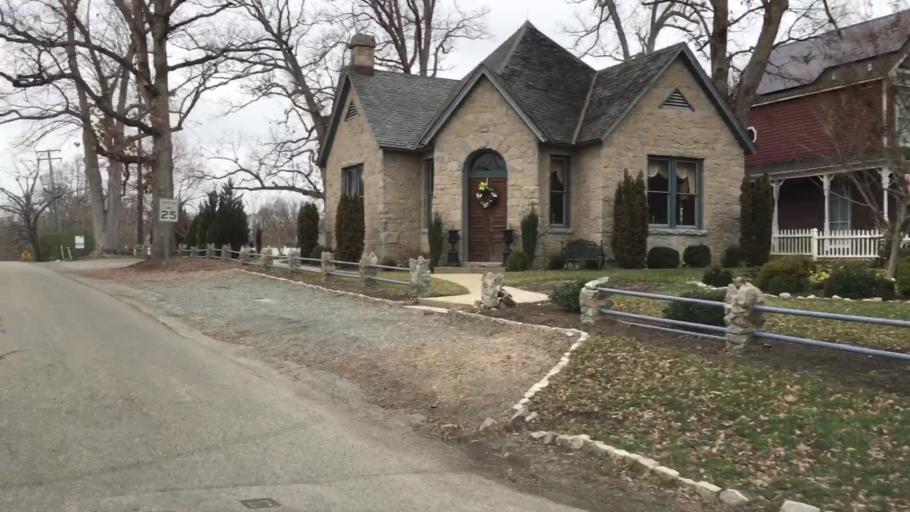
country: US
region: Virginia
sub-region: Chesterfield County
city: Bon Air
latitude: 37.5246
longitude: -77.5592
